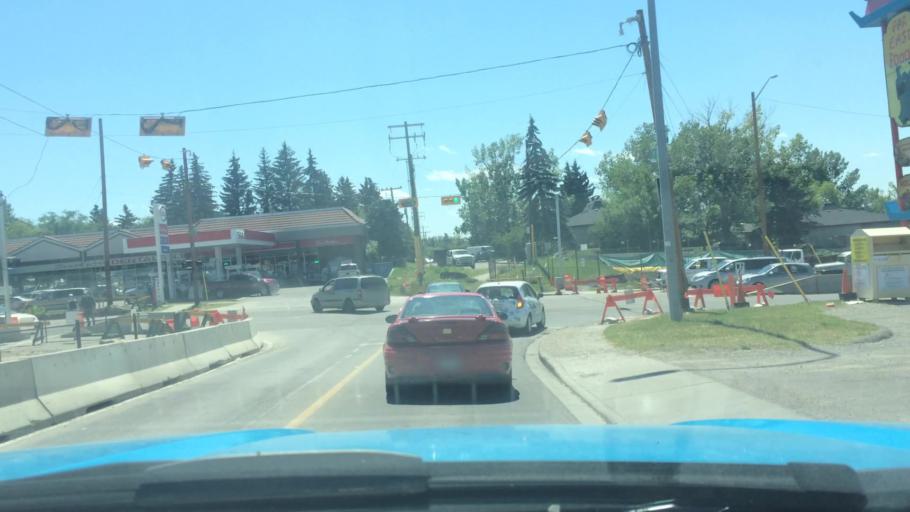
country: CA
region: Alberta
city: Calgary
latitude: 51.0382
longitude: -113.9932
